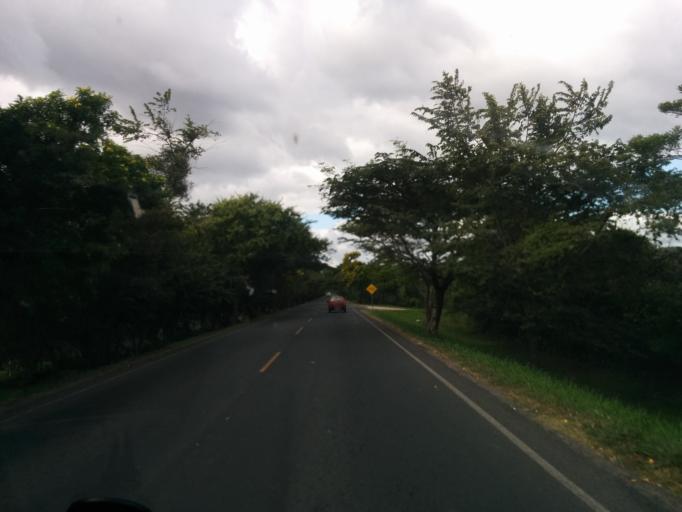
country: NI
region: Esteli
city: Esteli
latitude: 13.1389
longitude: -86.3666
